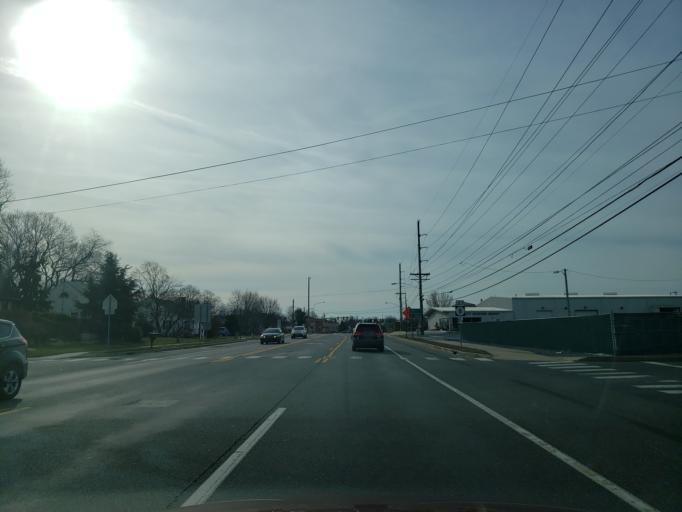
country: US
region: Delaware
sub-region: Kent County
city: Dover
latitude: 39.1610
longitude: -75.5436
